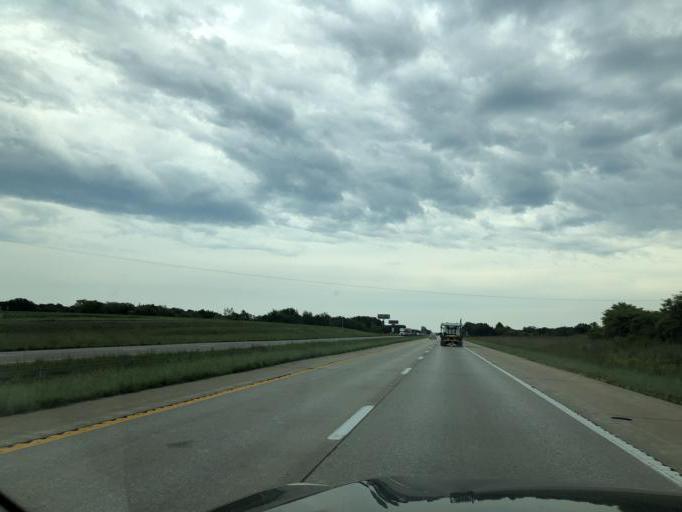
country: US
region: Missouri
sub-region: Montgomery County
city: Montgomery City
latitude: 38.9043
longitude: -91.6455
